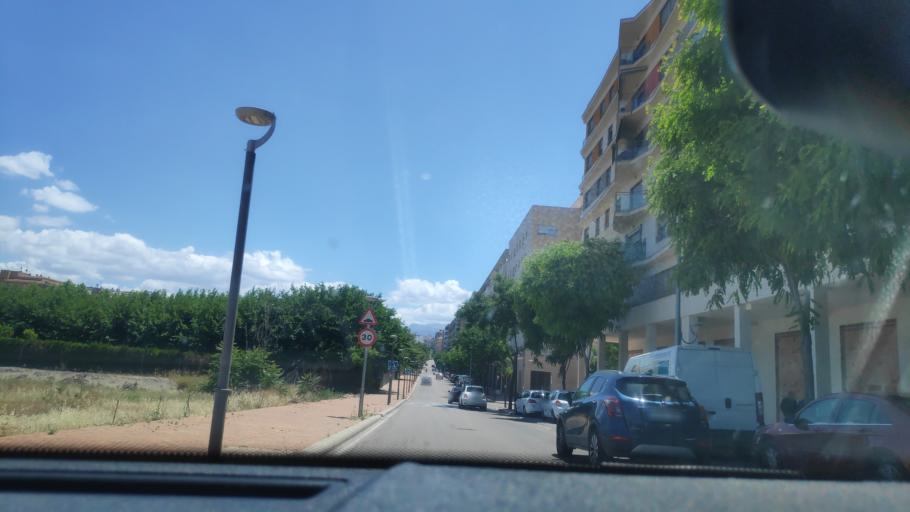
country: ES
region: Andalusia
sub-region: Provincia de Jaen
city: Jaen
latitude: 37.7901
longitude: -3.7920
